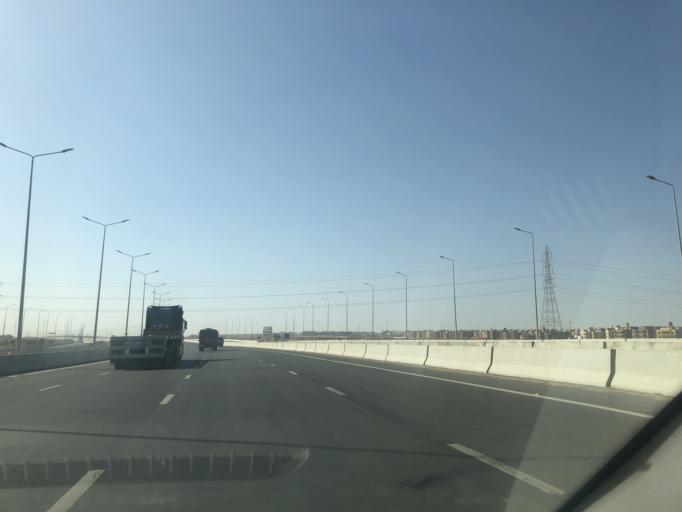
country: EG
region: Al Jizah
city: Madinat Sittah Uktubar
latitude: 29.9647
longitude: 30.8876
